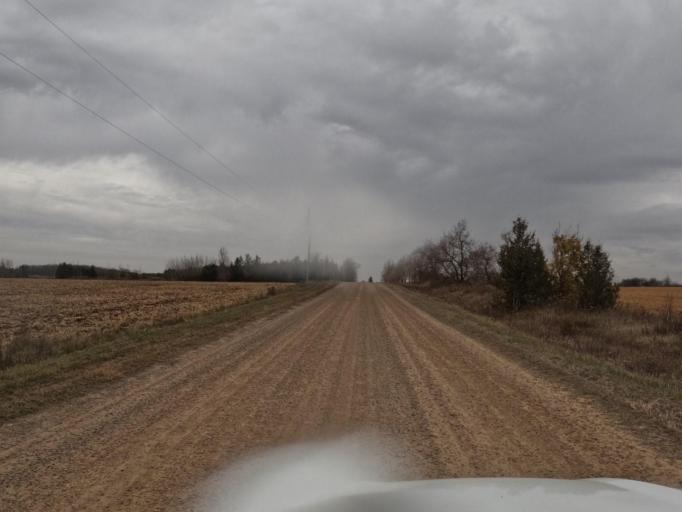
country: CA
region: Ontario
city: Shelburne
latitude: 43.8703
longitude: -80.3786
